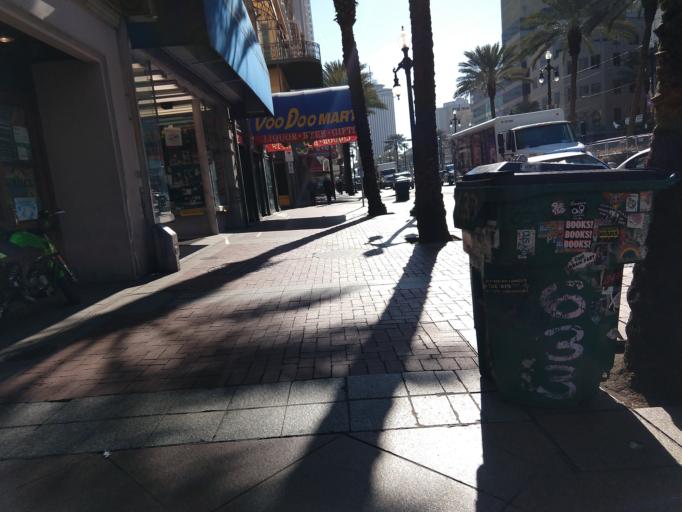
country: US
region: Louisiana
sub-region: Orleans Parish
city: New Orleans
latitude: 29.9531
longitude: -90.0688
